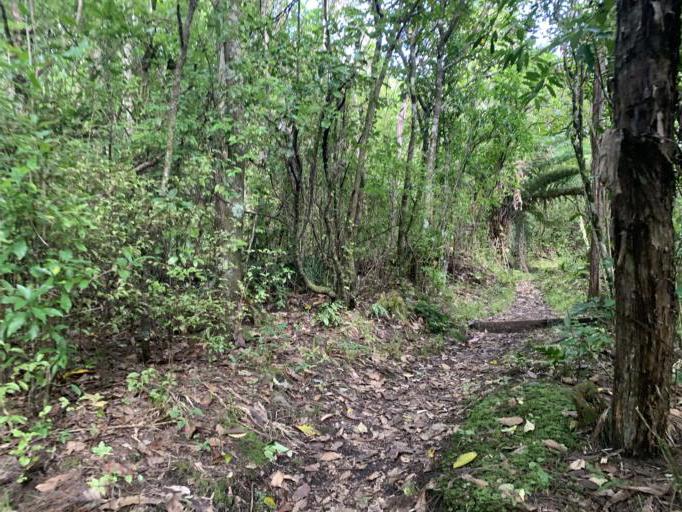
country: NZ
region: Waikato
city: Turangi
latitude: -38.9727
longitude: 175.7757
